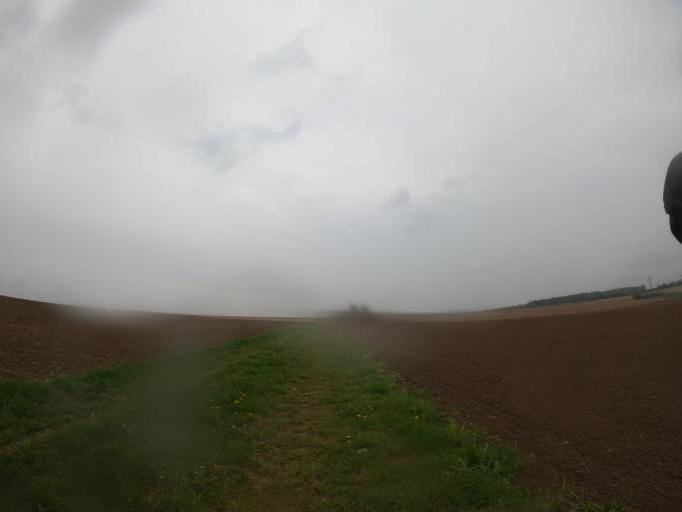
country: DE
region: Baden-Wuerttemberg
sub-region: Regierungsbezirk Stuttgart
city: Hemmingen
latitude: 48.8873
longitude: 9.0240
